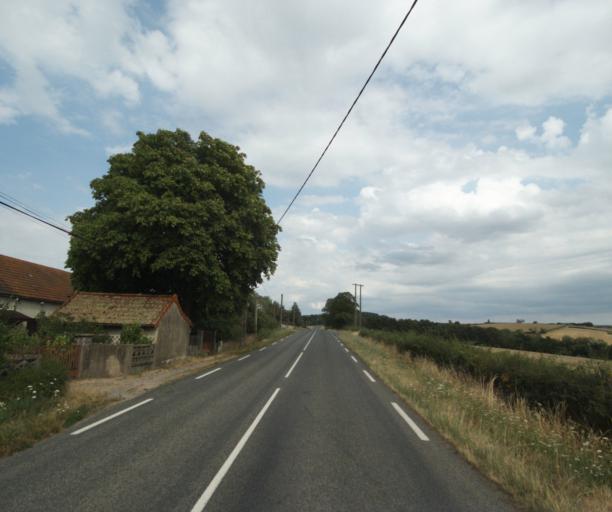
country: FR
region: Bourgogne
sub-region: Departement de Saone-et-Loire
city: Gueugnon
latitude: 46.6011
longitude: 4.0962
